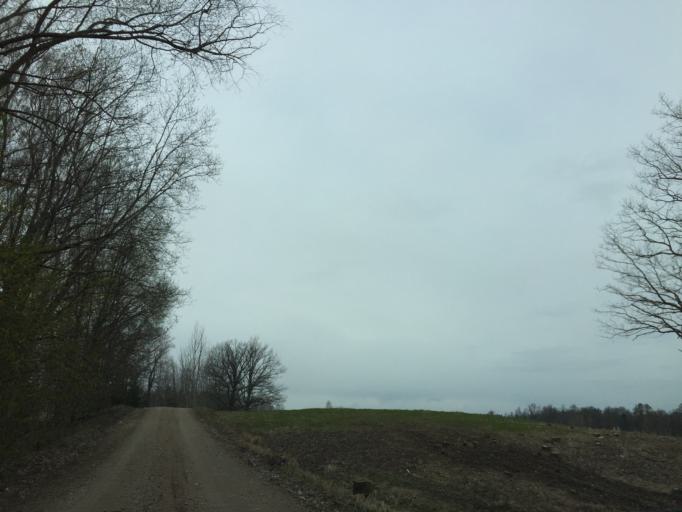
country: LV
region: Amatas Novads
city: Drabesi
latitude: 57.2570
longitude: 25.2957
